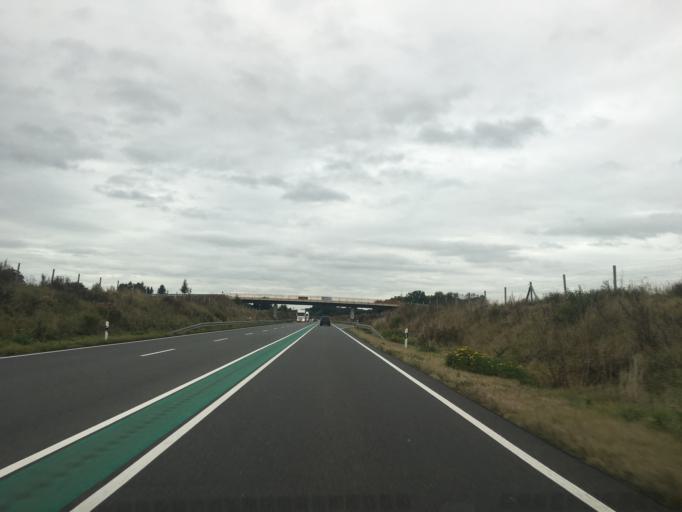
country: DE
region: North Rhine-Westphalia
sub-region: Regierungsbezirk Munster
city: Steinfurt
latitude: 52.1669
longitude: 7.3016
